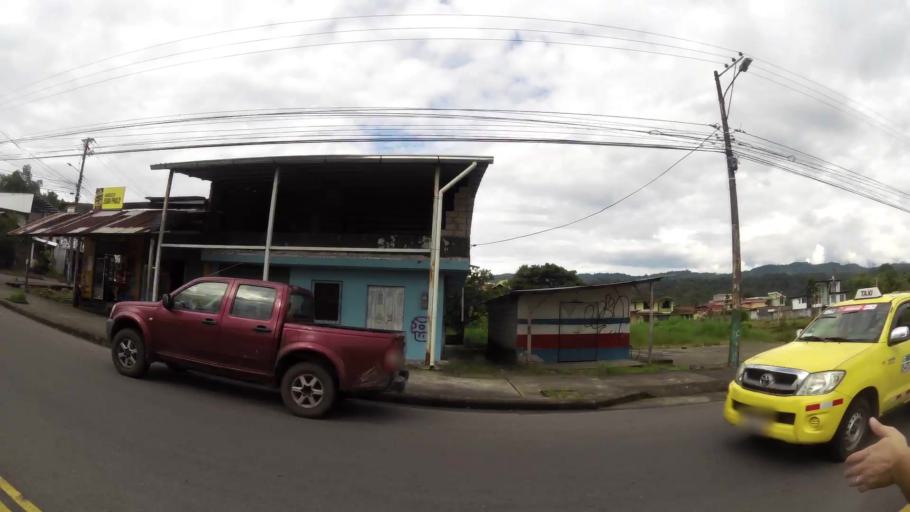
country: EC
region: Pastaza
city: Puyo
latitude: -1.4759
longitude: -78.0005
